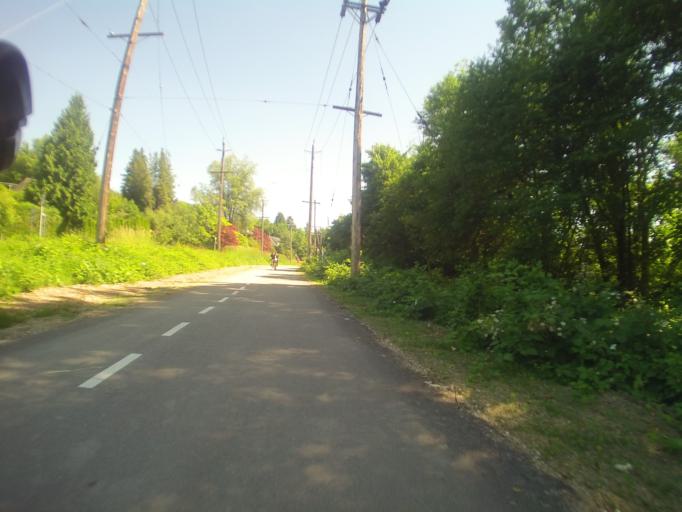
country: CA
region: British Columbia
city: Vancouver
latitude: 49.2443
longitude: -123.1477
